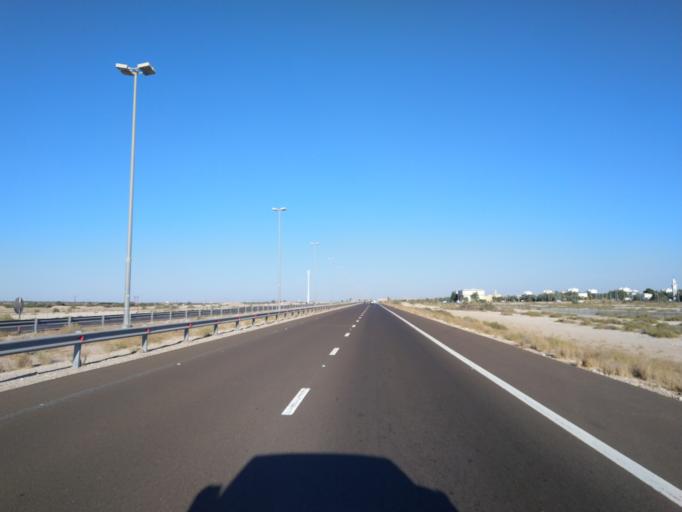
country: OM
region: Al Buraimi
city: Al Buraymi
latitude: 24.5220
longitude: 55.5321
